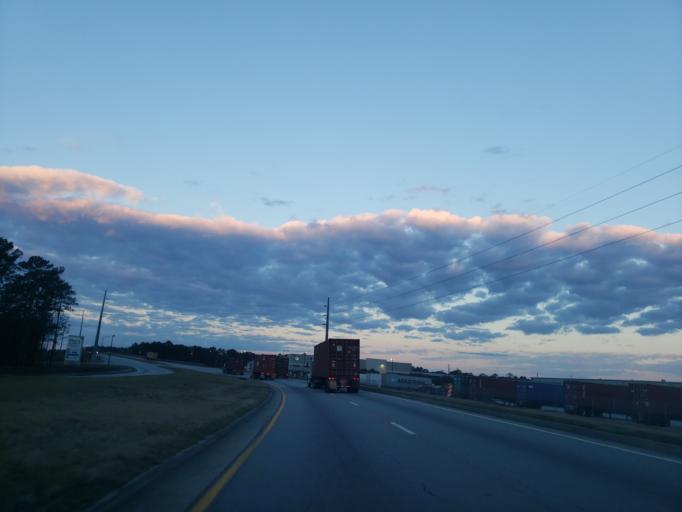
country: US
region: Georgia
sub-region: Chatham County
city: Port Wentworth
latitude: 32.1646
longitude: -81.1952
